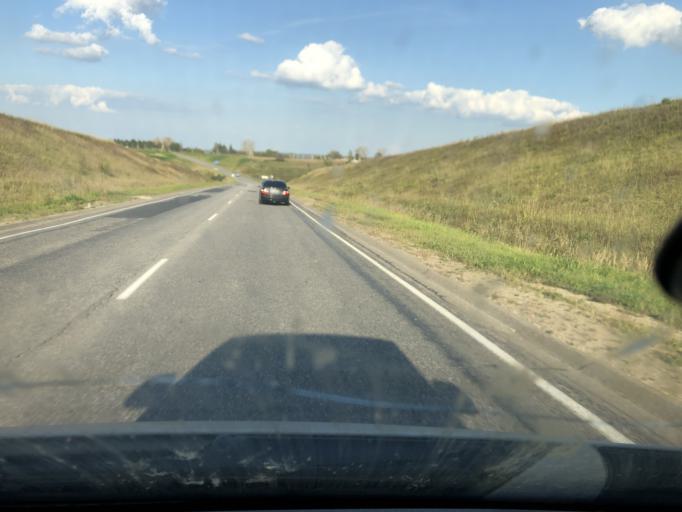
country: RU
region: Kaluga
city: Kozel'sk
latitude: 54.0872
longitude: 35.8344
